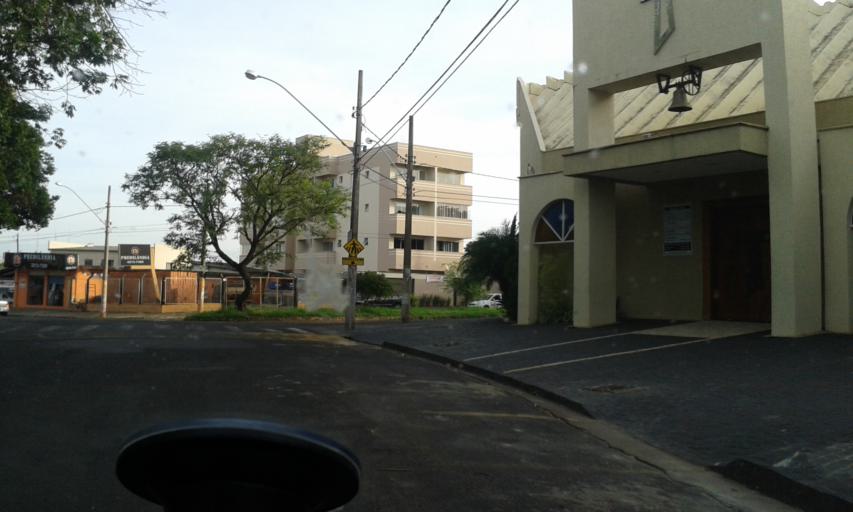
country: BR
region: Minas Gerais
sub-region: Uberlandia
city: Uberlandia
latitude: -18.9012
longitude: -48.2505
